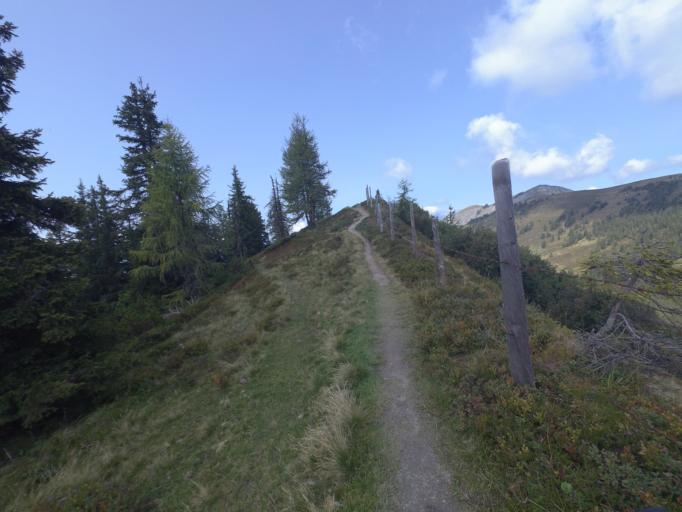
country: AT
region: Salzburg
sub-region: Politischer Bezirk Sankt Johann im Pongau
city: Kleinarl
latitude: 47.2692
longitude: 13.2760
